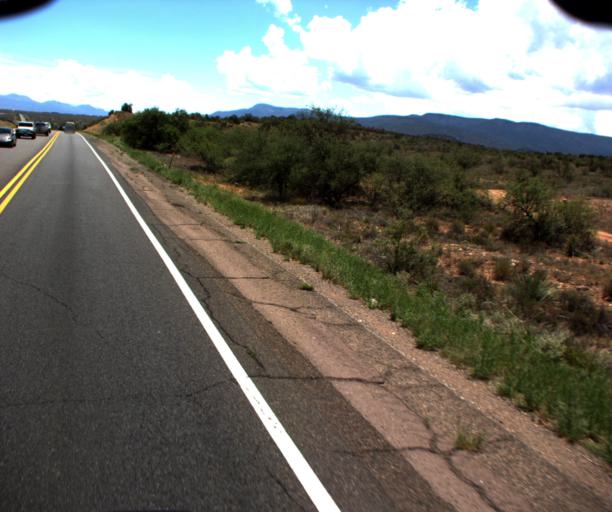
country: US
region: Arizona
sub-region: Yavapai County
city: Cornville
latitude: 34.6498
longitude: -111.9560
